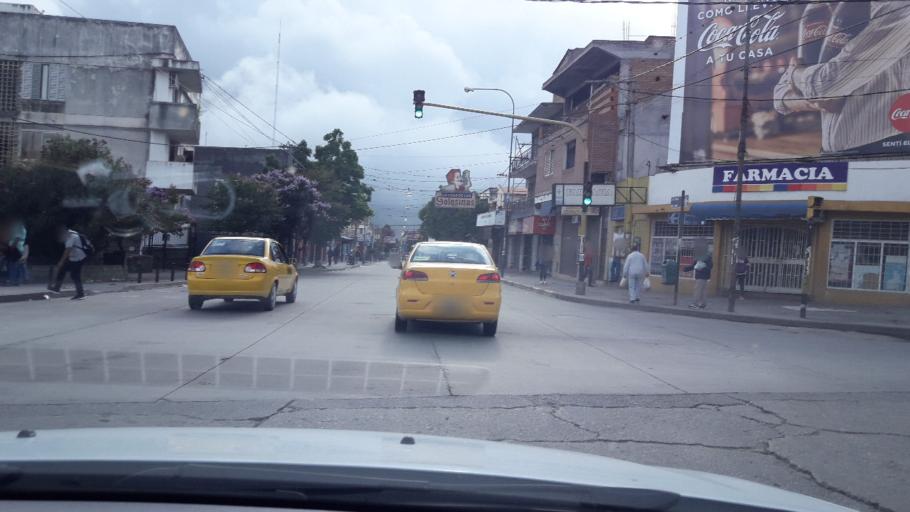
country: AR
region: Jujuy
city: San Salvador de Jujuy
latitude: -24.1910
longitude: -65.3025
